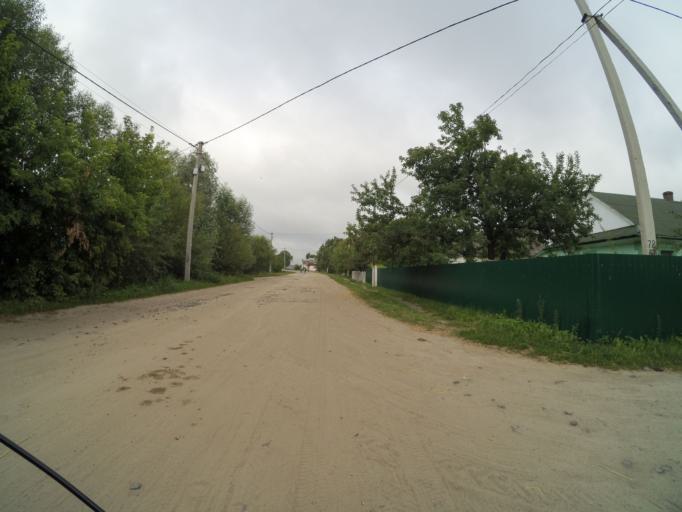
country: UA
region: Volyn
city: Shats'k
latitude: 51.5464
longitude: 23.9377
